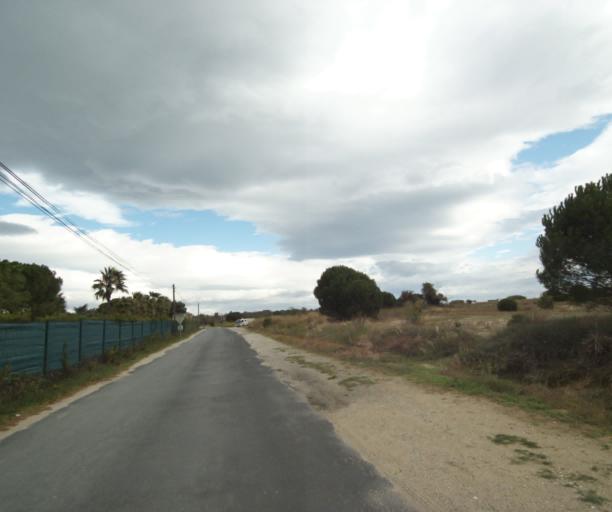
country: FR
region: Languedoc-Roussillon
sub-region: Departement des Pyrenees-Orientales
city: Argelers
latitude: 42.5710
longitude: 3.0412
